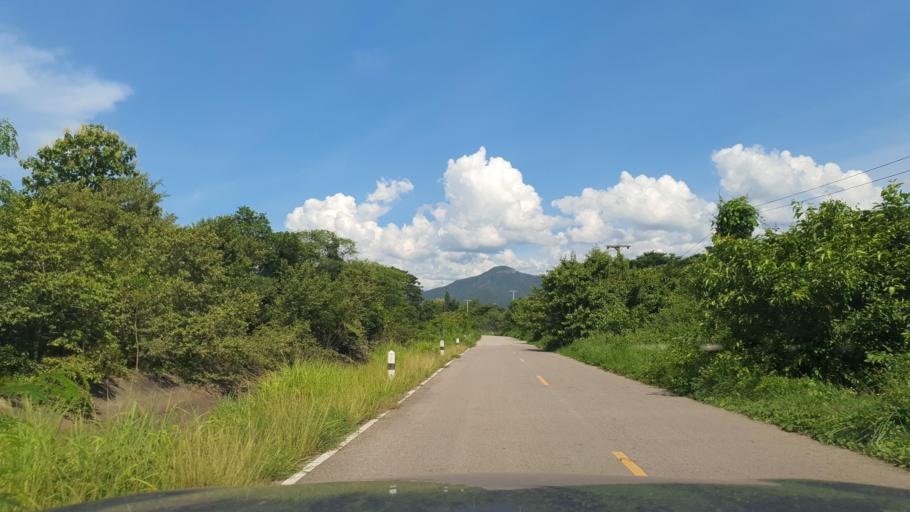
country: TH
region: Chiang Mai
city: Mae On
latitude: 18.7448
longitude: 99.1922
